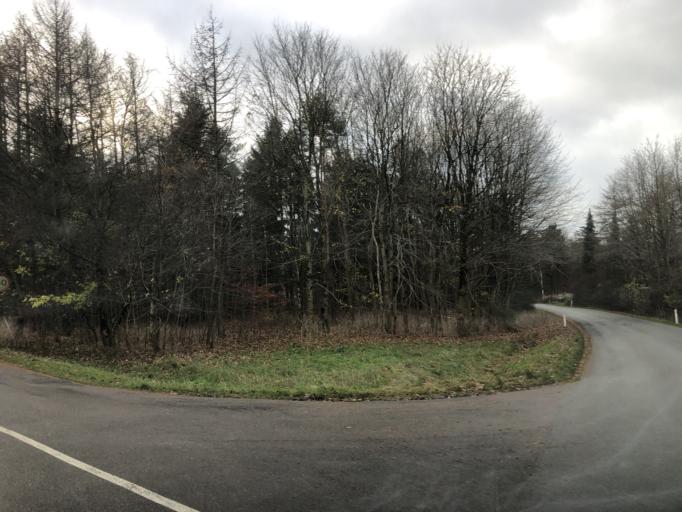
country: DK
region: North Denmark
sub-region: Alborg Kommune
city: Svenstrup
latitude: 56.9346
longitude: 9.8044
